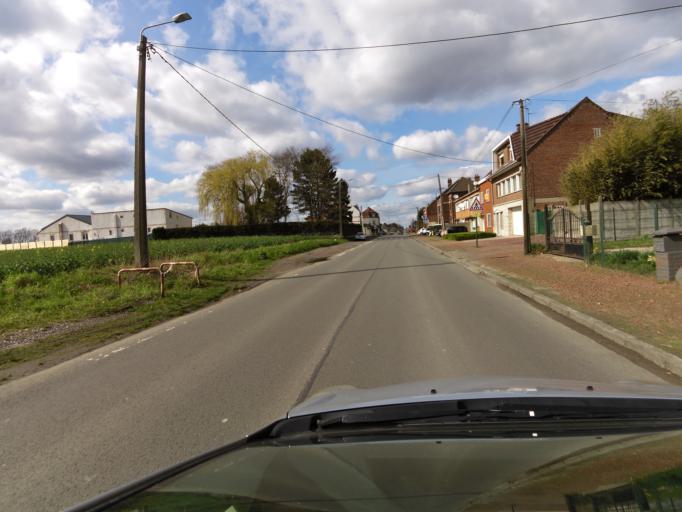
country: FR
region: Nord-Pas-de-Calais
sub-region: Departement du Pas-de-Calais
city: Violaines
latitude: 50.5503
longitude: 2.7938
